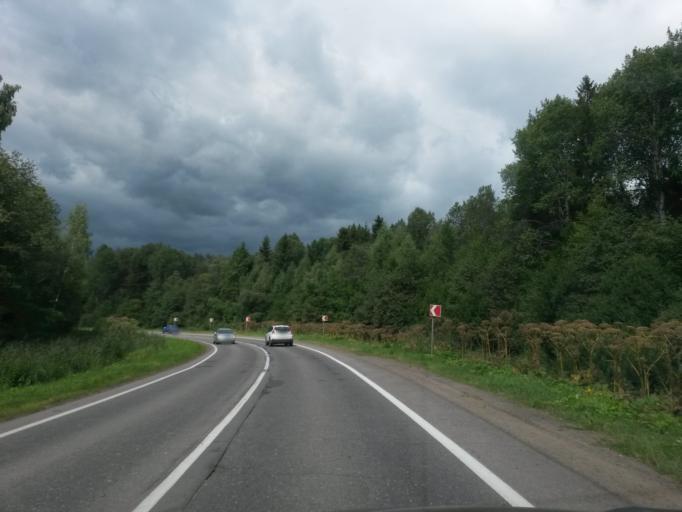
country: RU
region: Jaroslavl
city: Yaroslavl
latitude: 57.8005
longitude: 39.8270
